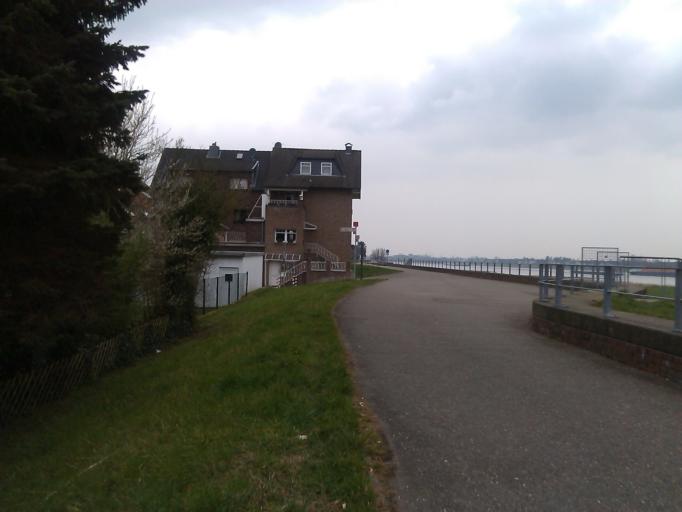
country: DE
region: North Rhine-Westphalia
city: Monheim am Rhein
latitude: 51.0484
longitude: 6.9225
